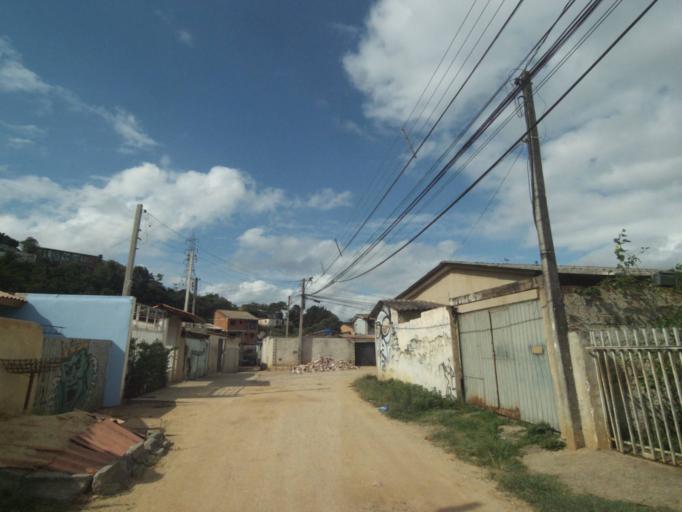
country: BR
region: Parana
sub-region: Almirante Tamandare
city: Almirante Tamandare
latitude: -25.3792
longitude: -49.3000
